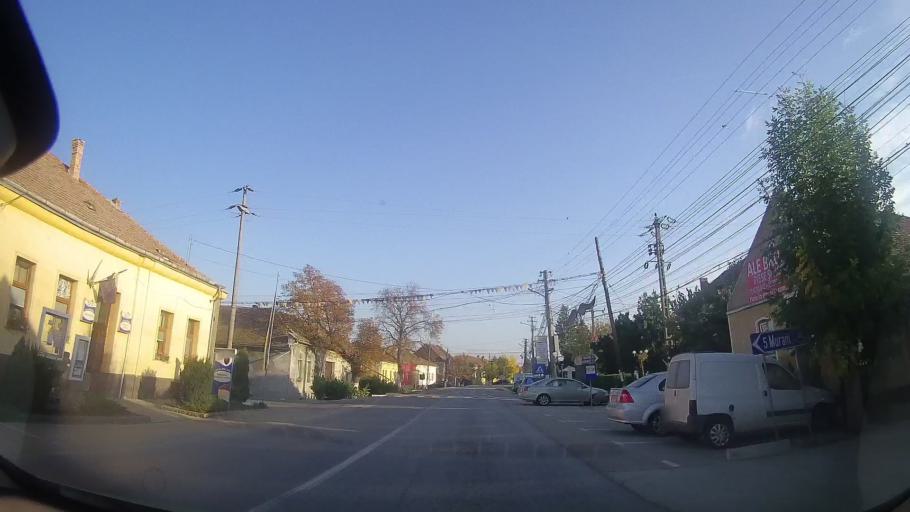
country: RO
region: Timis
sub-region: Comuna Pischia
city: Pischia
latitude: 45.9035
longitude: 21.3400
